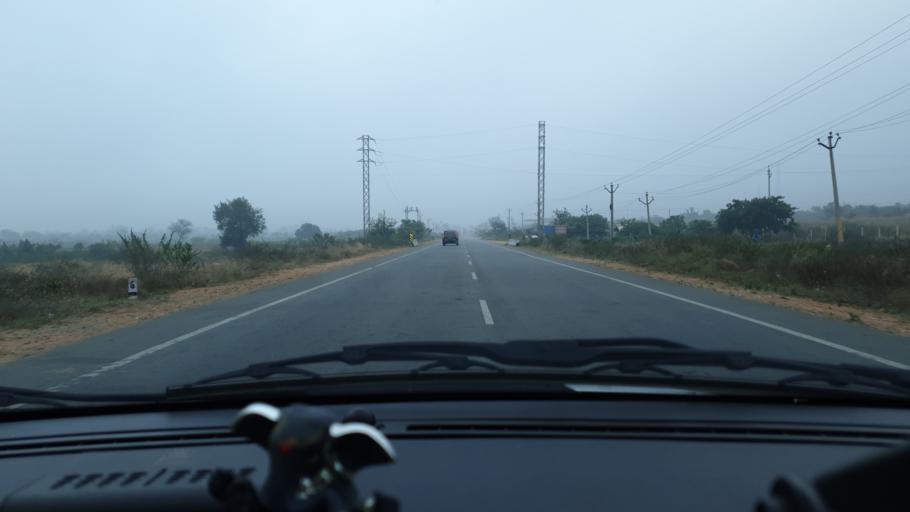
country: IN
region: Telangana
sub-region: Mahbubnagar
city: Farrukhnagar
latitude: 16.9331
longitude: 78.5284
